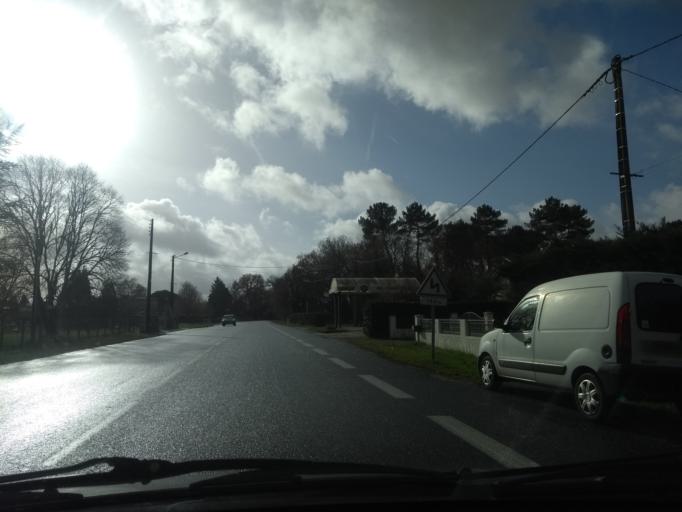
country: FR
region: Aquitaine
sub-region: Departement de la Gironde
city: Belin-Beliet
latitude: 44.4994
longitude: -0.7902
